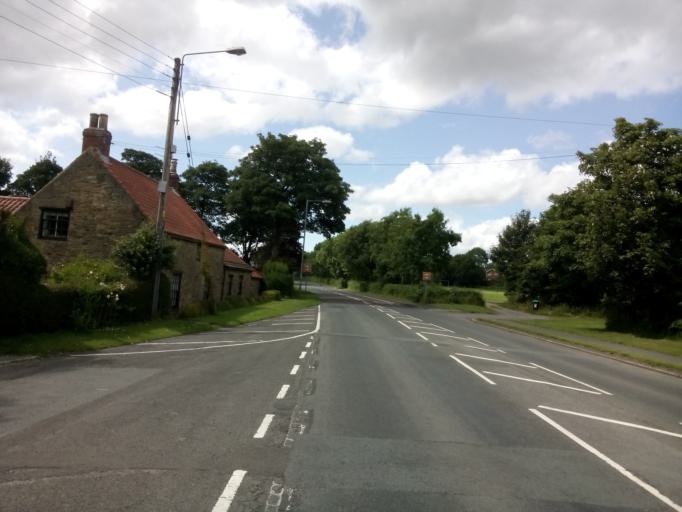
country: GB
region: England
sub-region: County Durham
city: Ushaw Moor
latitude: 54.7713
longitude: -1.6246
